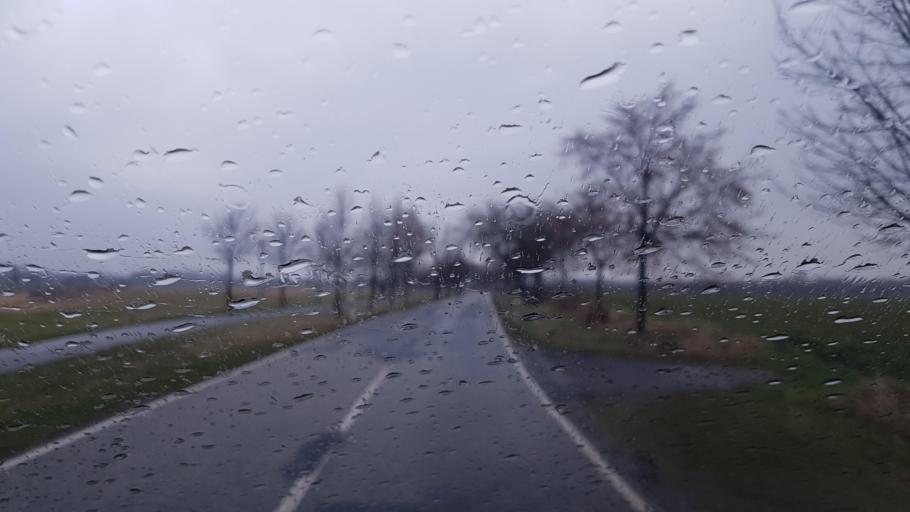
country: DE
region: Brandenburg
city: Zehdenick
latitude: 52.9653
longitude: 13.3060
